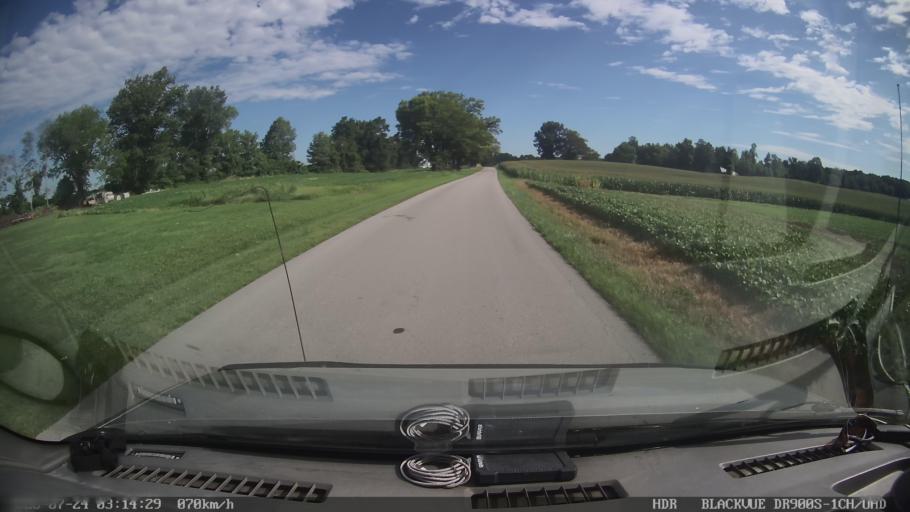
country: US
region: Kentucky
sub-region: Todd County
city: Guthrie
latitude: 36.6872
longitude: -87.1718
